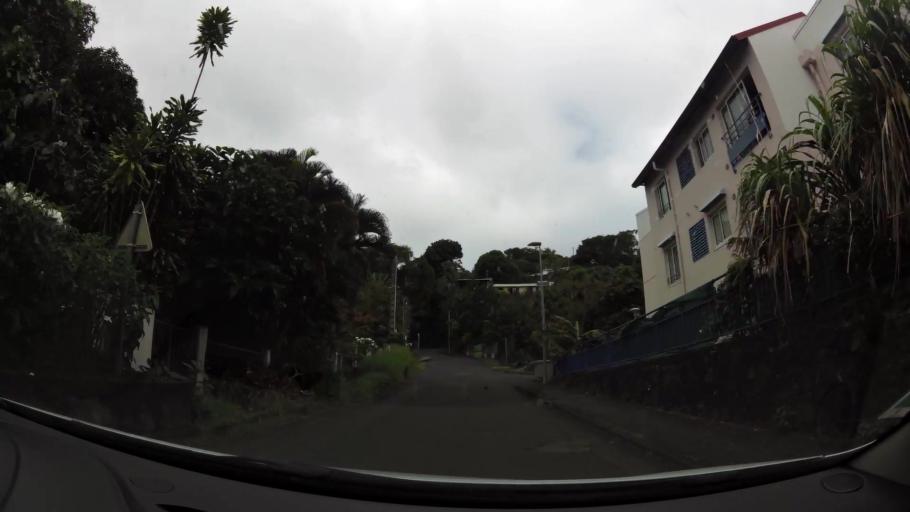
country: RE
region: Reunion
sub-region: Reunion
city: Sainte-Marie
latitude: -20.8983
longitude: 55.5492
